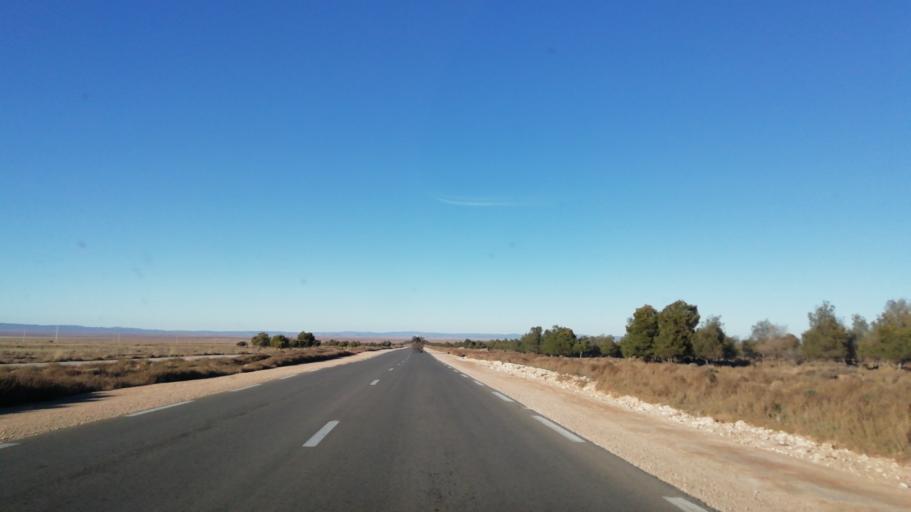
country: DZ
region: Tlemcen
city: Sebdou
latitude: 34.3186
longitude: -1.2630
